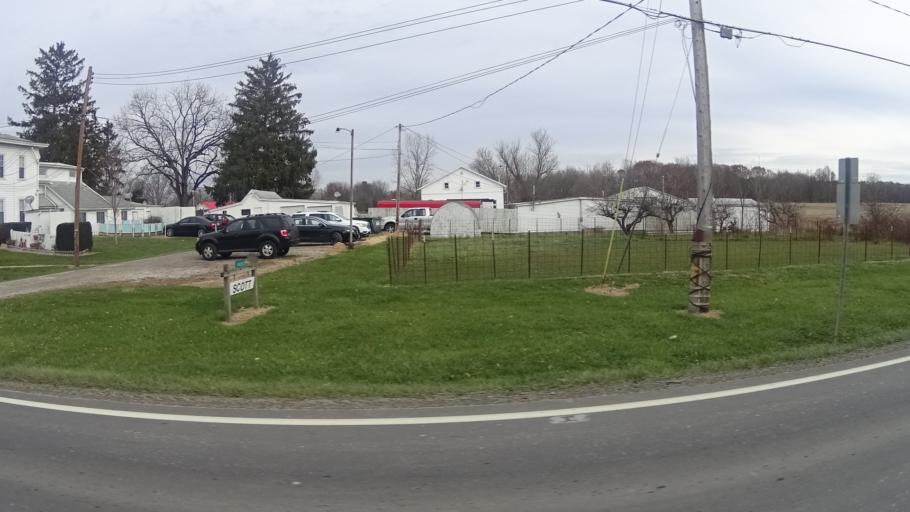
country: US
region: Ohio
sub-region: Cuyahoga County
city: Olmsted Falls
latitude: 41.3107
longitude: -81.9149
